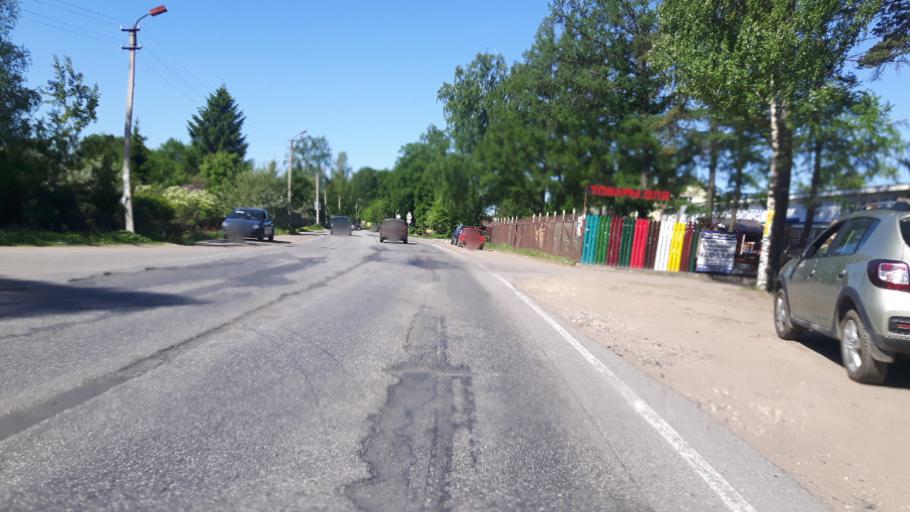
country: RU
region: Leningrad
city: Lebyazh'ye
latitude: 59.9607
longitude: 29.4309
